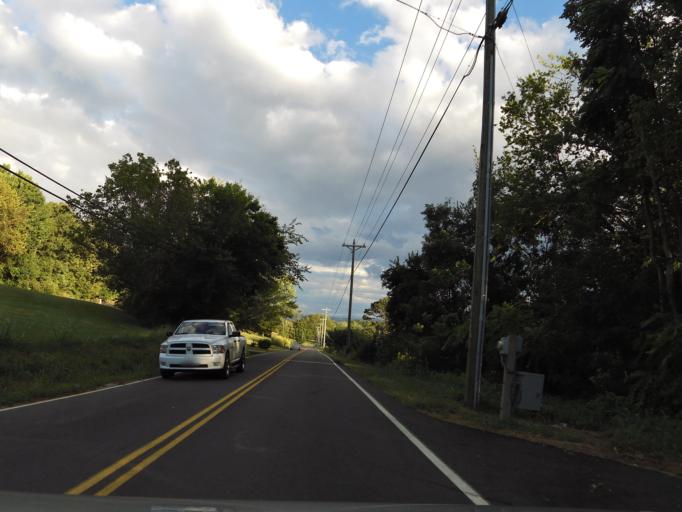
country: US
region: Tennessee
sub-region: Grainger County
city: Rutledge
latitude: 36.2118
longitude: -83.5019
